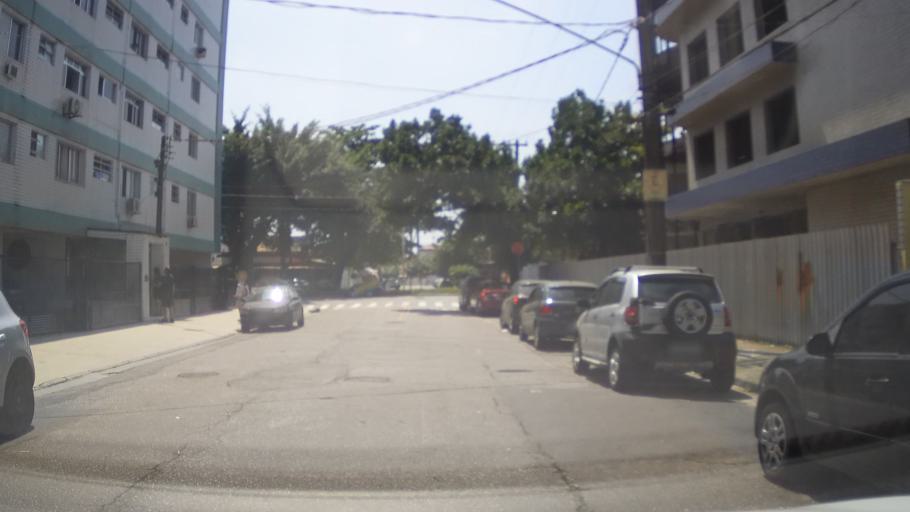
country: BR
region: Sao Paulo
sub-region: Santos
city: Santos
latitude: -23.9770
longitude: -46.2983
